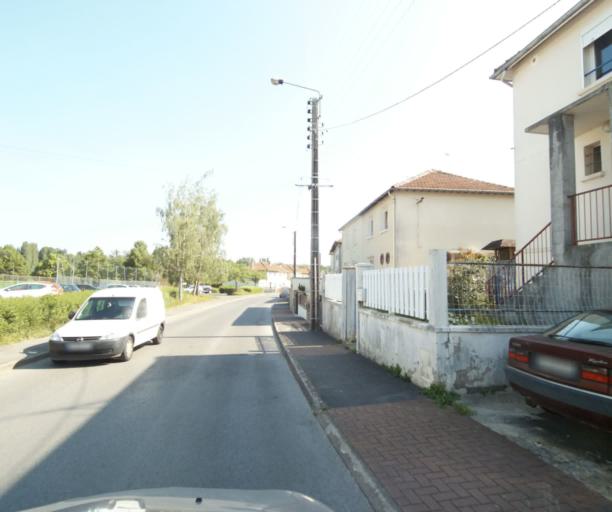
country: FR
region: Champagne-Ardenne
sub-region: Departement des Ardennes
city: Charleville-Mezieres
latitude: 49.7799
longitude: 4.7030
